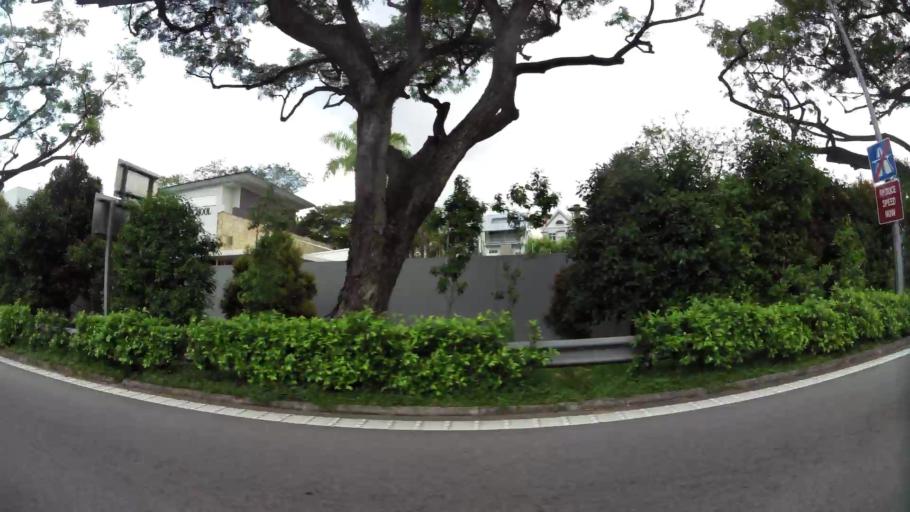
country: SG
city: Singapore
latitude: 1.3462
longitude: 103.8597
